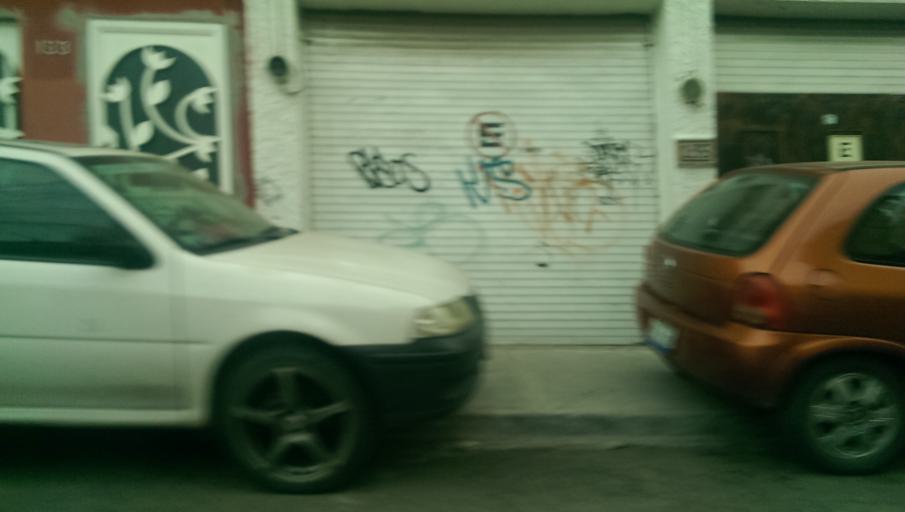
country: MX
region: Queretaro
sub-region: Queretaro
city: Santiago de Queretaro
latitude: 20.6012
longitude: -100.3631
